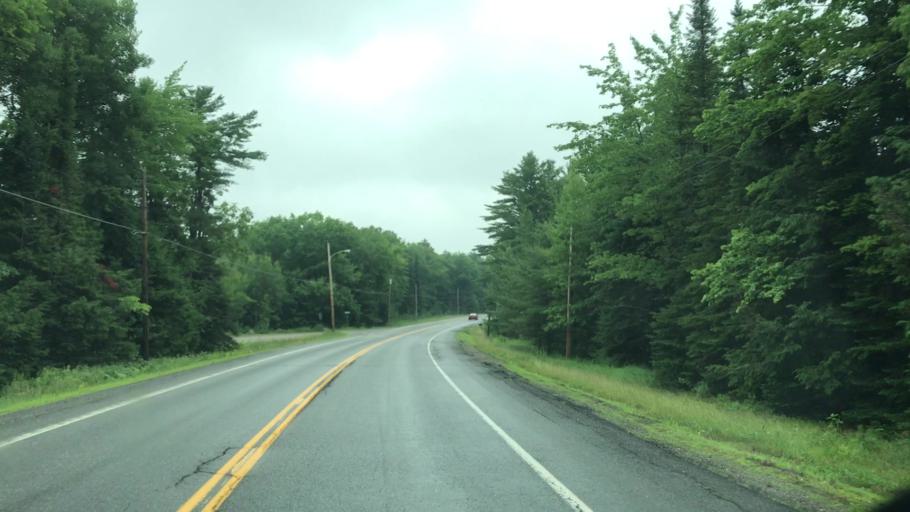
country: US
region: Maine
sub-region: Penobscot County
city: Howland
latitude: 45.2698
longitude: -68.6387
